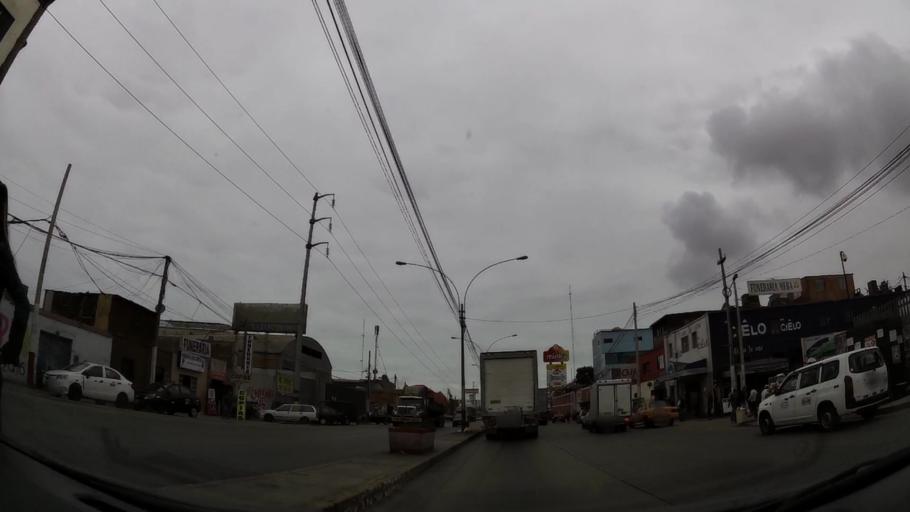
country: PE
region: Callao
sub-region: Callao
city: Callao
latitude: -12.0492
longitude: -77.1081
